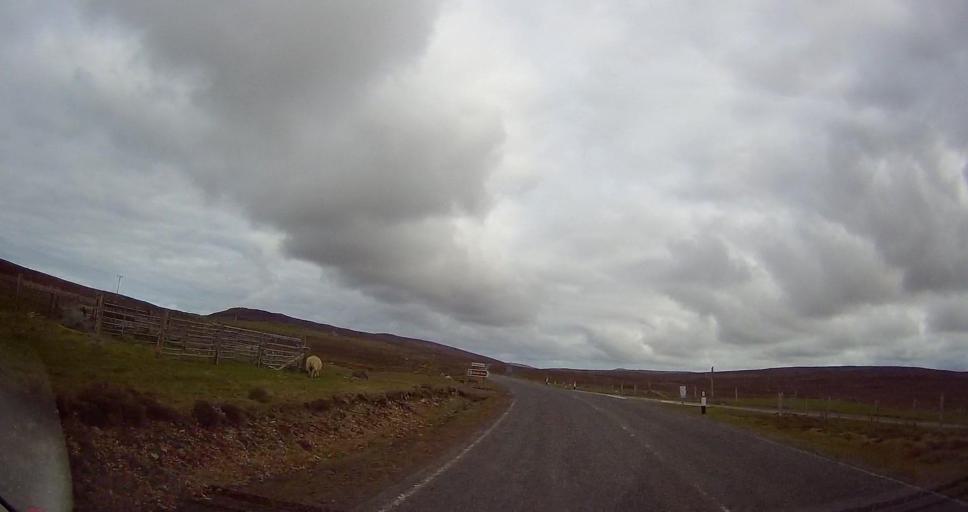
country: GB
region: Scotland
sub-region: Shetland Islands
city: Shetland
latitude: 60.6995
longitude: -0.9208
